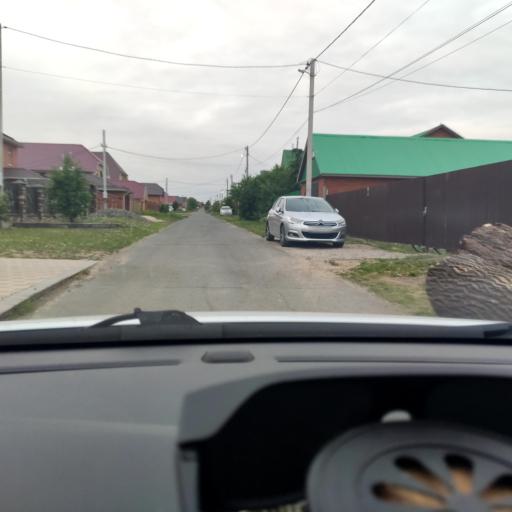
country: RU
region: Tatarstan
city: Vysokaya Gora
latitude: 55.9137
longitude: 49.3331
